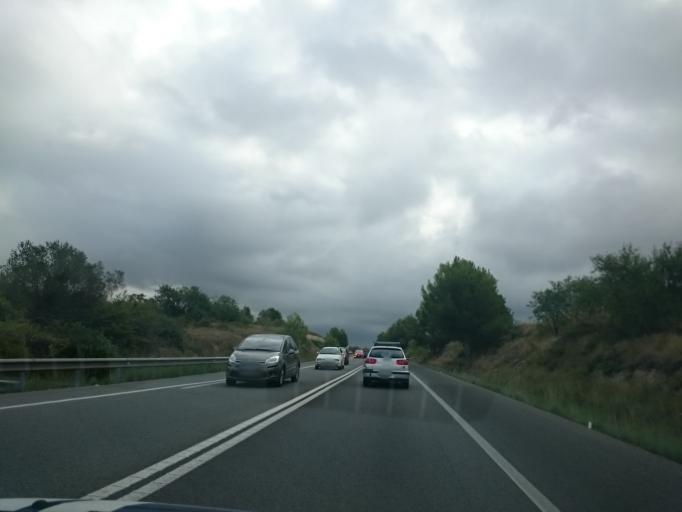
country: ES
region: Catalonia
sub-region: Provincia de Barcelona
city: Vilanova i la Geltru
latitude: 41.2364
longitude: 1.7377
